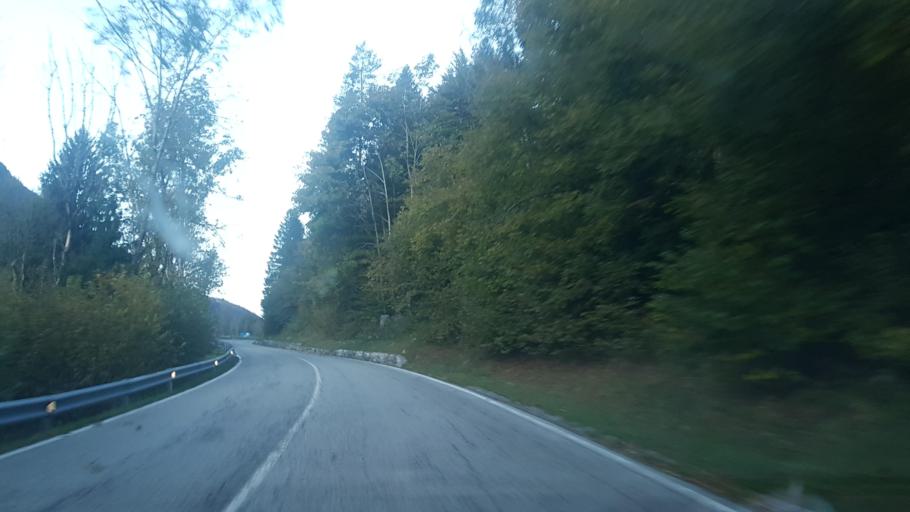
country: IT
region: Friuli Venezia Giulia
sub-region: Provincia di Udine
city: Chiaulis
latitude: 46.3625
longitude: 12.9476
